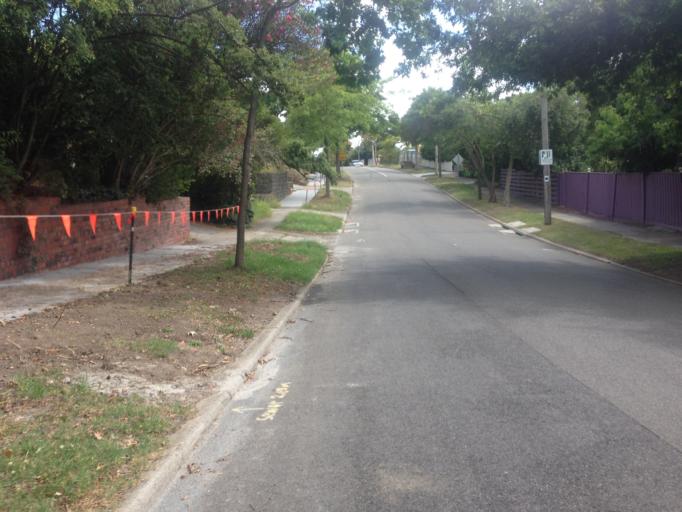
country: AU
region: Victoria
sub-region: Boroondara
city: Balwyn North
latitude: -37.7907
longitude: 145.0820
